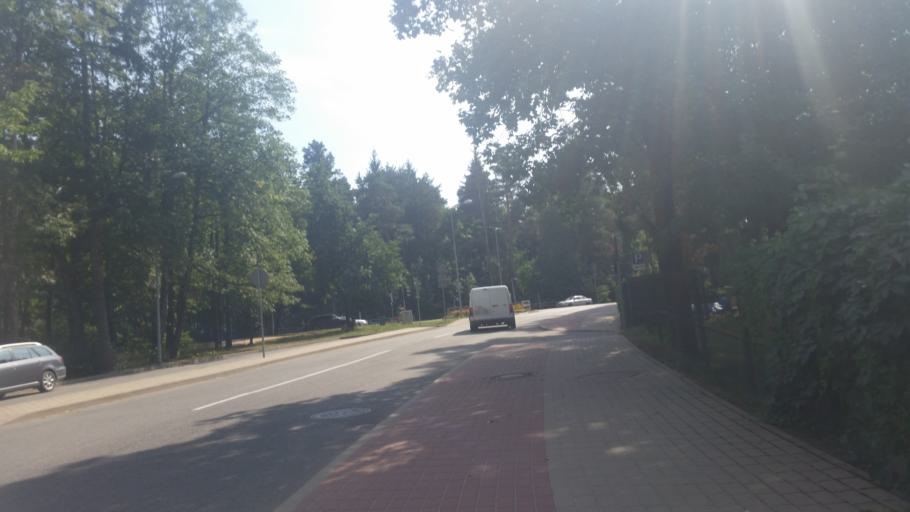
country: LV
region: Ogre
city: Ogre
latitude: 56.8208
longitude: 24.6115
